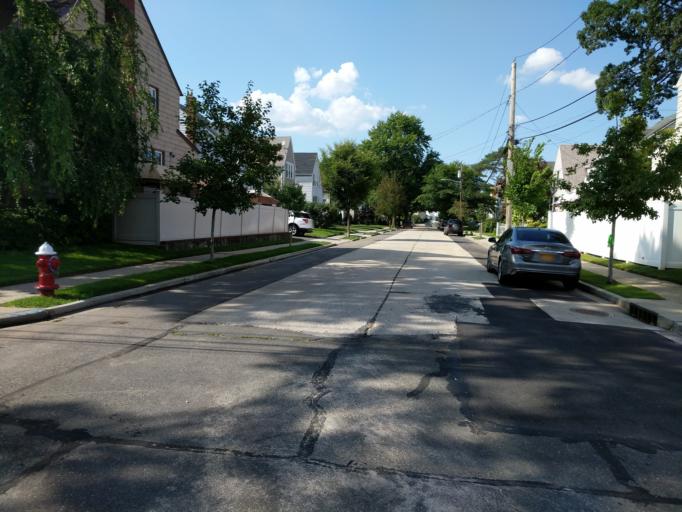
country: US
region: New York
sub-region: Nassau County
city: Hewlett
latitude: 40.6499
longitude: -73.6958
